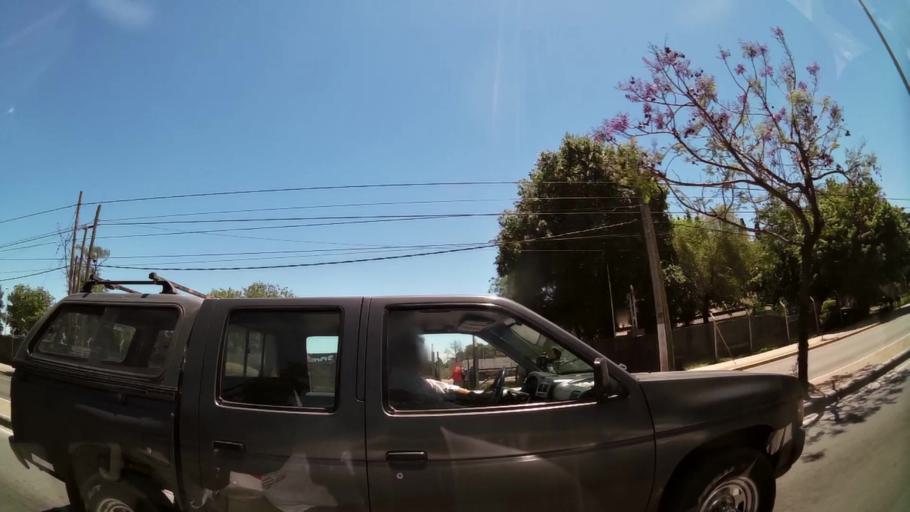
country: AR
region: Buenos Aires
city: Hurlingham
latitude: -34.4989
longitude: -58.7099
